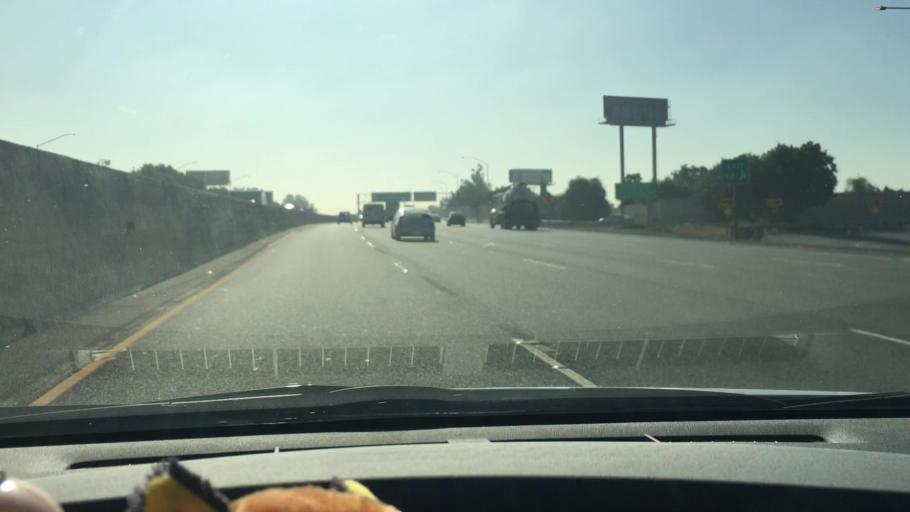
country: US
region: California
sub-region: Los Angeles County
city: East Rancho Dominguez
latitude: 33.8883
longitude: -118.1892
